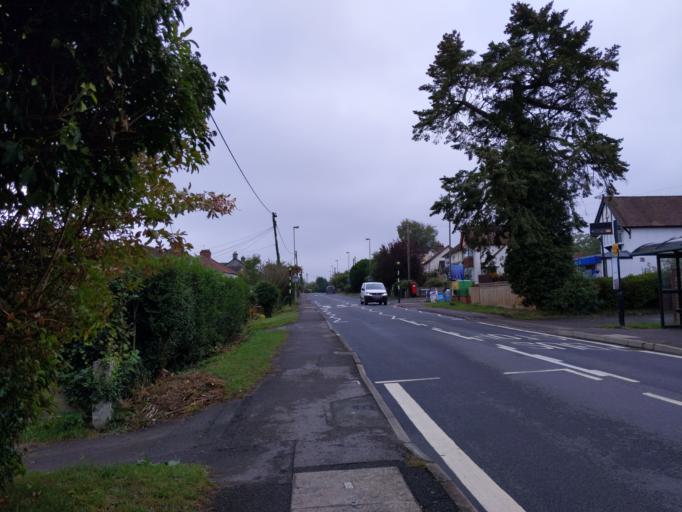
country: GB
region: England
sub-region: Oxfordshire
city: Oxford
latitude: 51.7227
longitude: -1.2478
